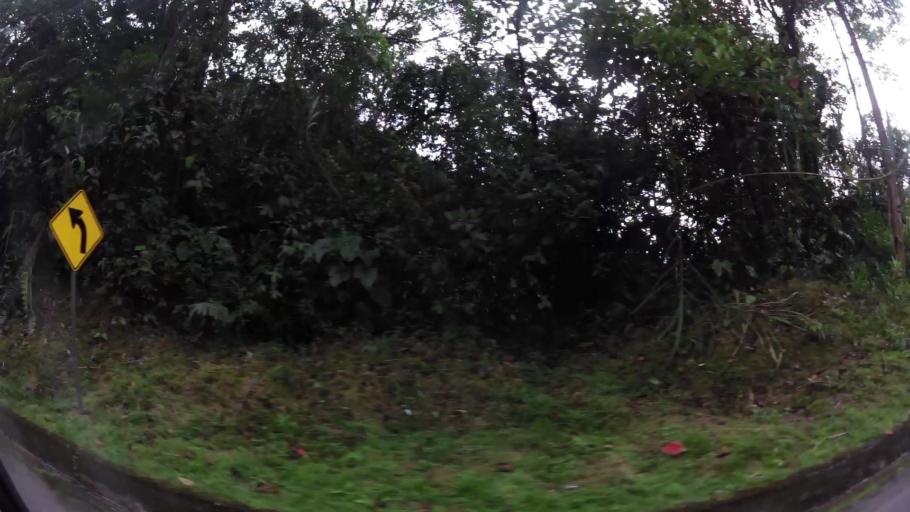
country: EC
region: Pastaza
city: Puyo
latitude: -1.4242
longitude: -78.1755
